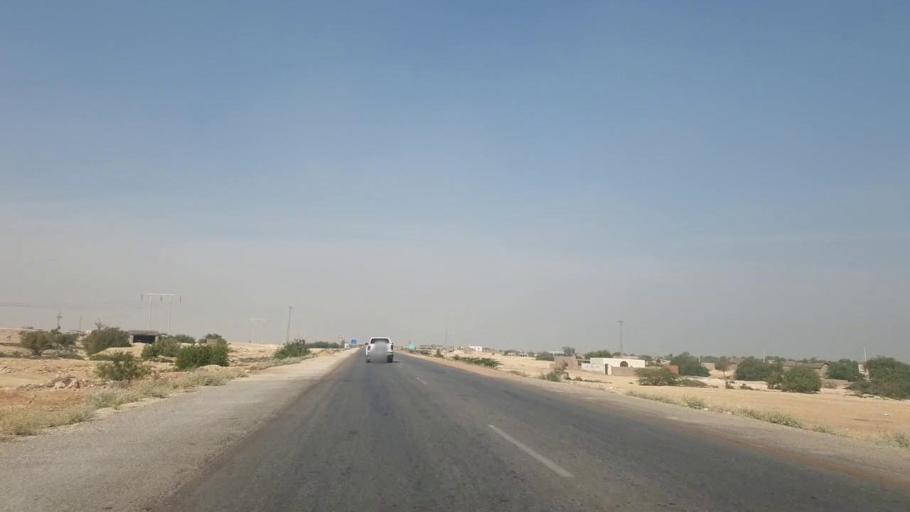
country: PK
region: Sindh
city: Hala
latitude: 25.7860
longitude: 68.2825
